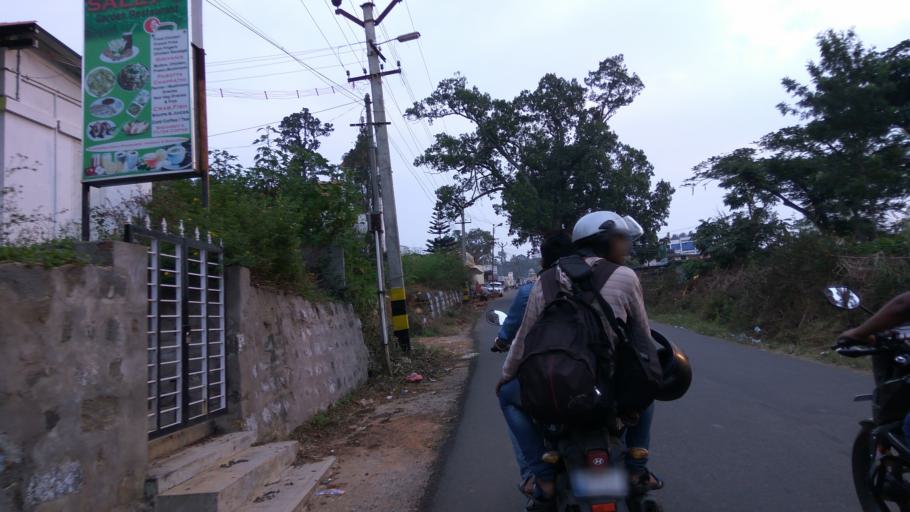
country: IN
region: Tamil Nadu
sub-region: Salem
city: Salem
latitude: 11.7778
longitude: 78.2096
